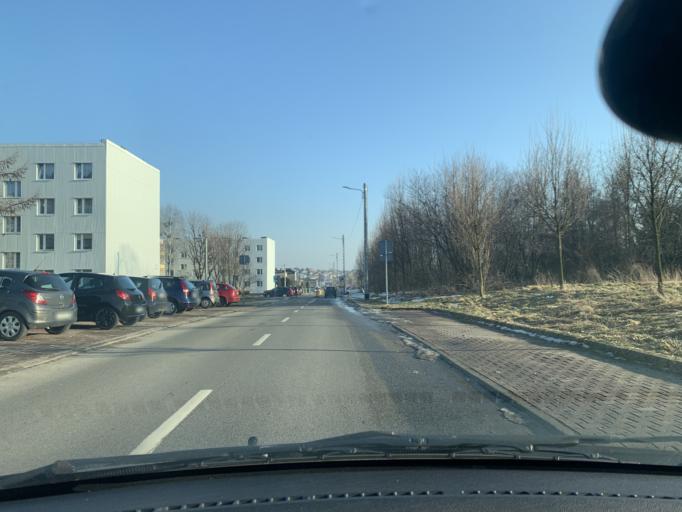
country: PL
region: Silesian Voivodeship
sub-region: Powiat tarnogorski
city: Radzionkow
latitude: 50.4052
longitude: 18.8947
